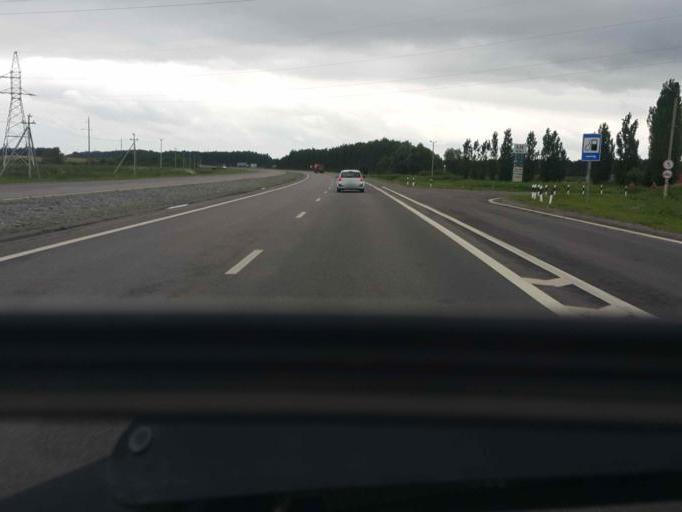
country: RU
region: Tambov
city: Zavoronezhskoye
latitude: 52.8733
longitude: 40.7551
